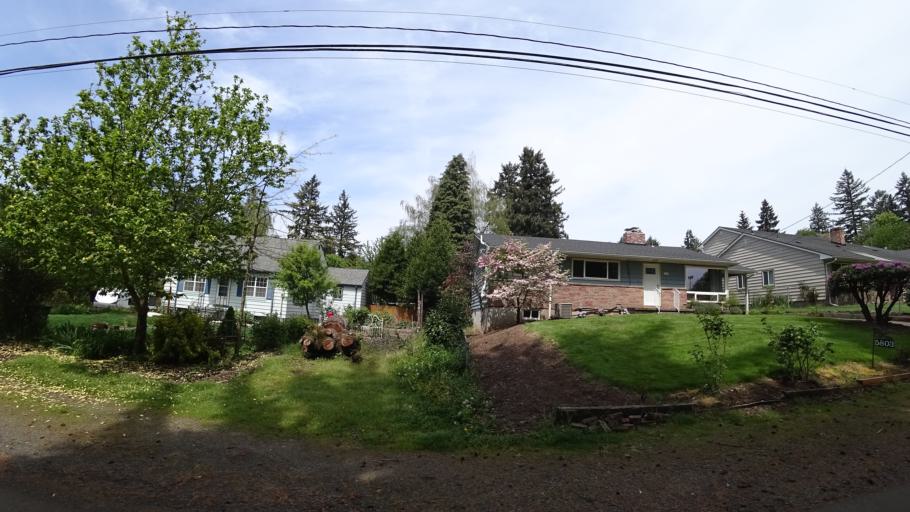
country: US
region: Oregon
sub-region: Clackamas County
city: Milwaukie
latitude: 45.4595
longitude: -122.6037
